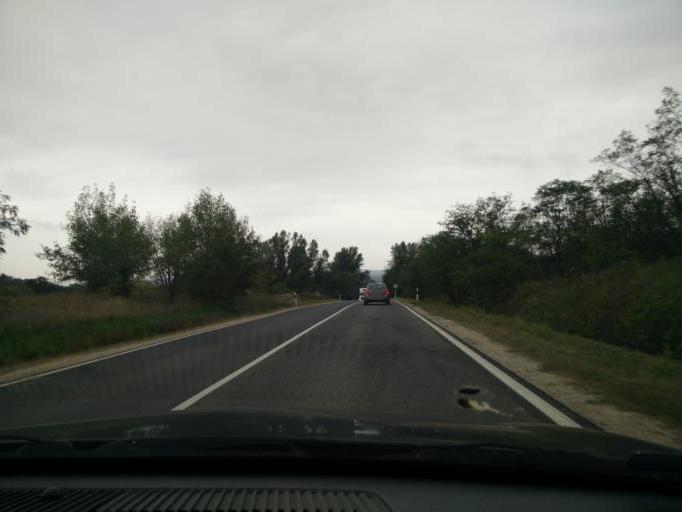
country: HU
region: Komarom-Esztergom
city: Kesztolc
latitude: 47.7124
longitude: 18.7714
